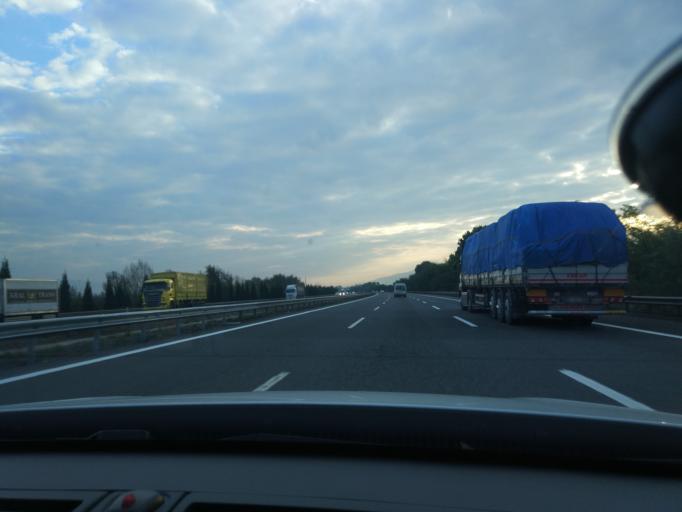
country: TR
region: Sakarya
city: Akyazi
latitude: 40.7427
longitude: 30.6639
